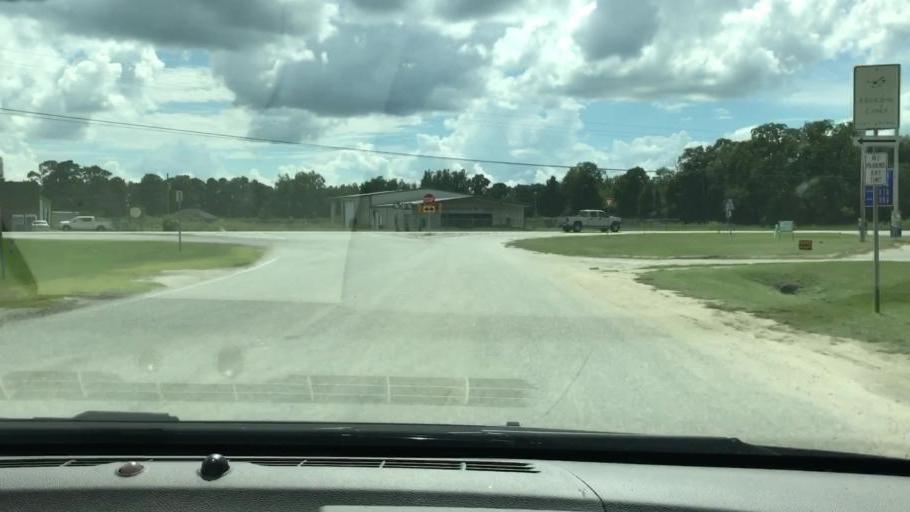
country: US
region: Georgia
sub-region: Quitman County
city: Georgetown
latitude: 31.8836
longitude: -85.0930
